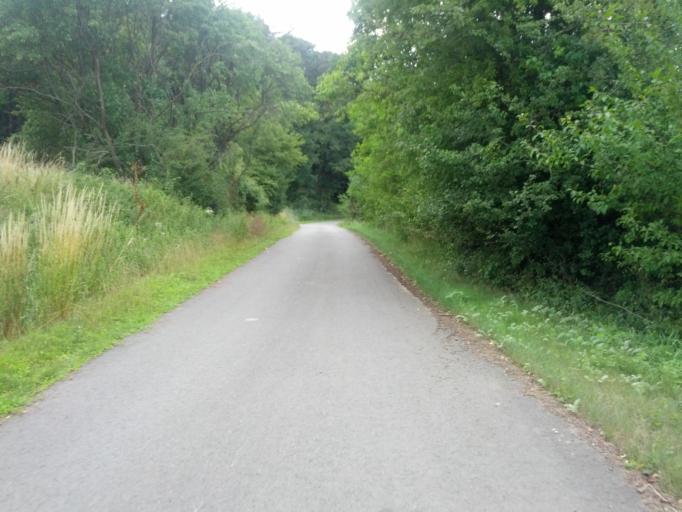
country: DE
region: Thuringia
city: Krauthausen
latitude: 51.0015
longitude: 10.2765
